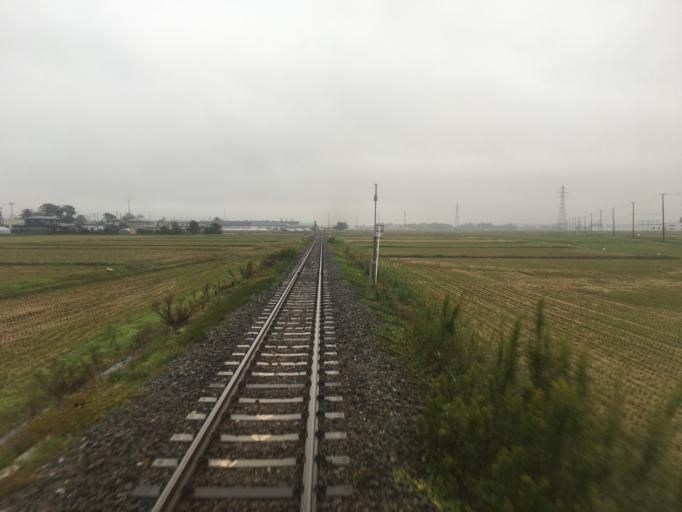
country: JP
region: Miyagi
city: Kogota
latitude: 38.5623
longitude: 141.0125
